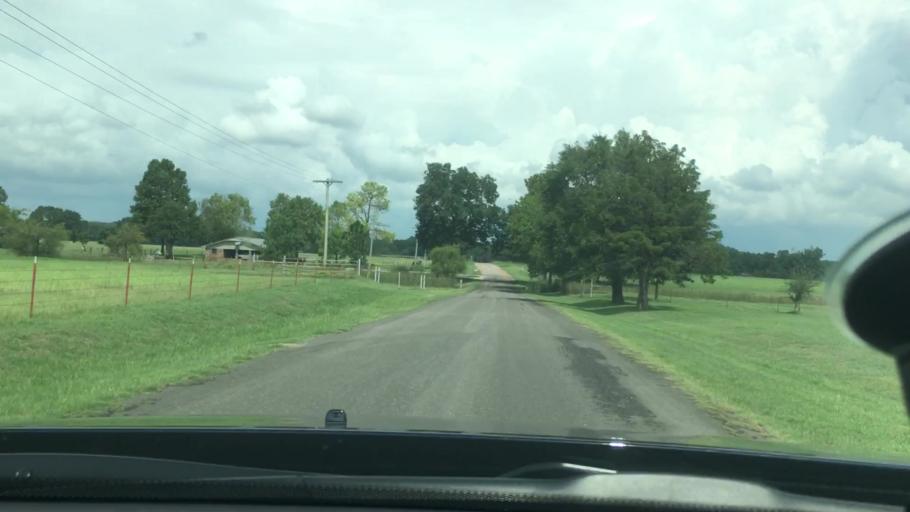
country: US
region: Oklahoma
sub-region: Carter County
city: Dickson
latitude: 34.2337
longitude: -96.9157
